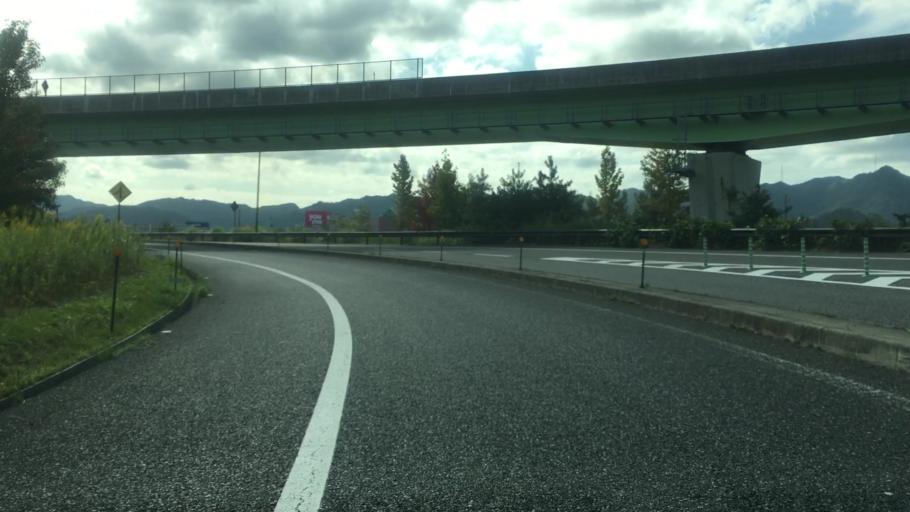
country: JP
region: Kyoto
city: Fukuchiyama
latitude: 35.1621
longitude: 135.0446
